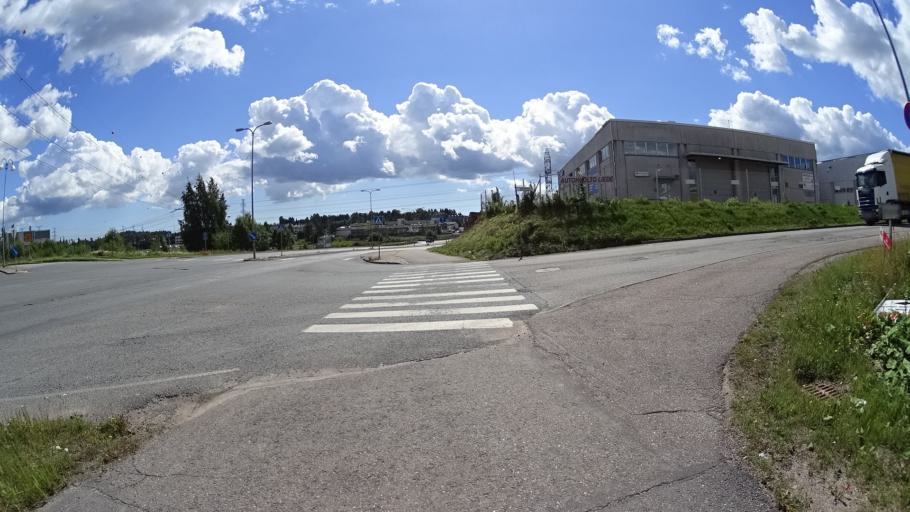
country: FI
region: Uusimaa
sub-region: Helsinki
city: Teekkarikylae
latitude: 60.3003
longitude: 24.8836
